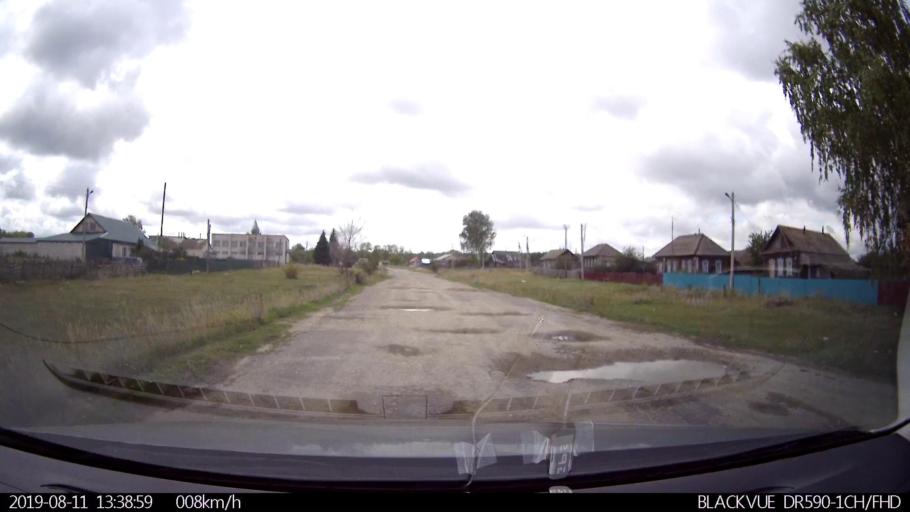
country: RU
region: Ulyanovsk
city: Ignatovka
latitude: 53.8596
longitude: 47.5796
